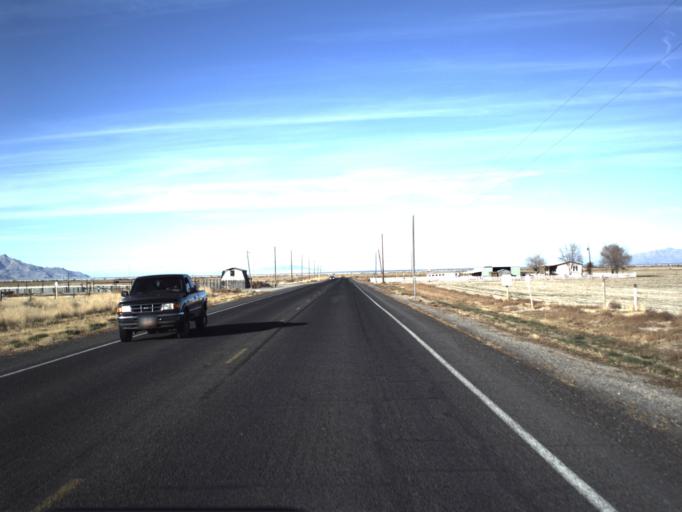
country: US
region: Utah
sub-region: Tooele County
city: Erda
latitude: 40.6073
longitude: -112.3708
